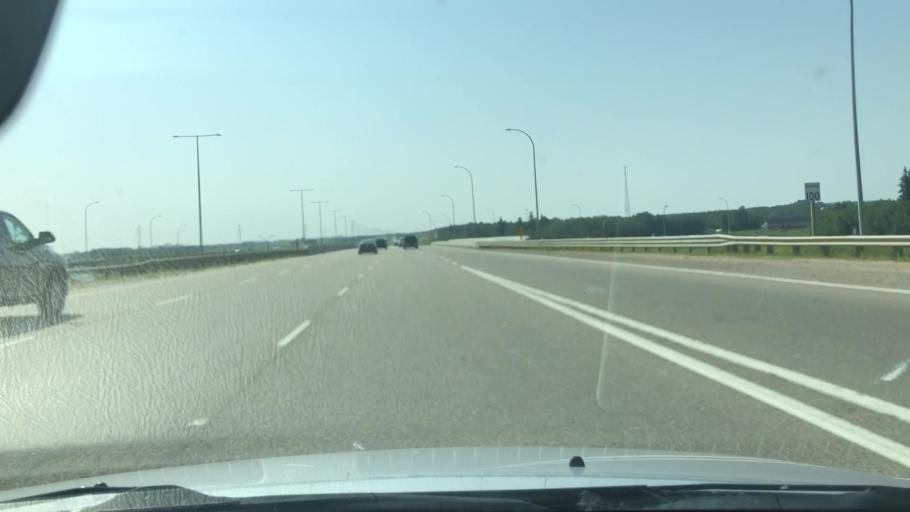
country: CA
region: Alberta
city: St. Albert
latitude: 53.5396
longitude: -113.6595
